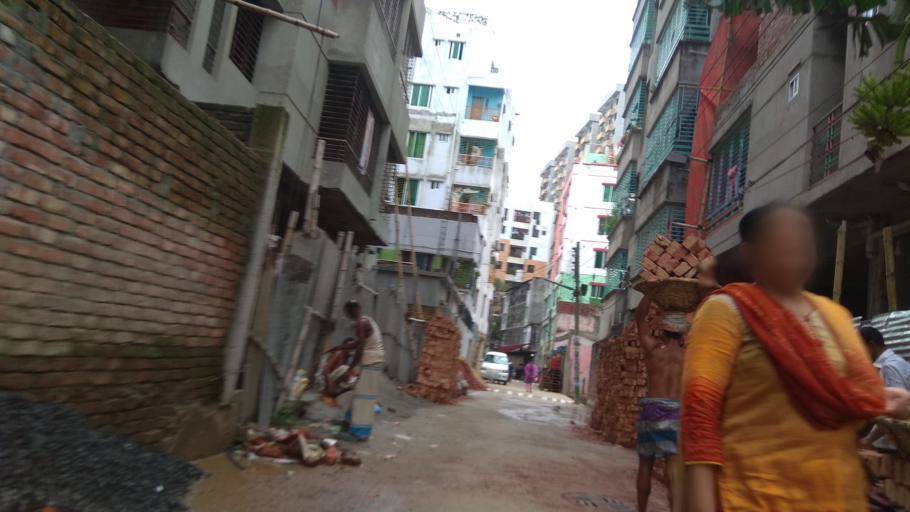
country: BD
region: Dhaka
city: Azimpur
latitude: 23.8003
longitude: 90.3605
